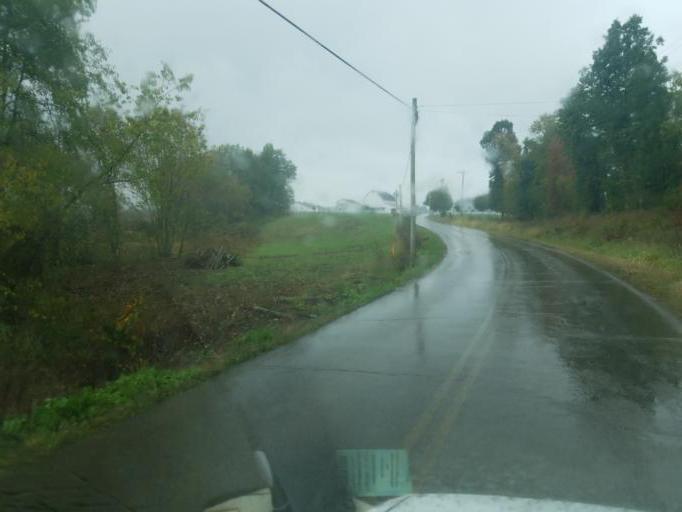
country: US
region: Ohio
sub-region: Wayne County
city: Shreve
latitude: 40.6399
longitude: -82.0206
